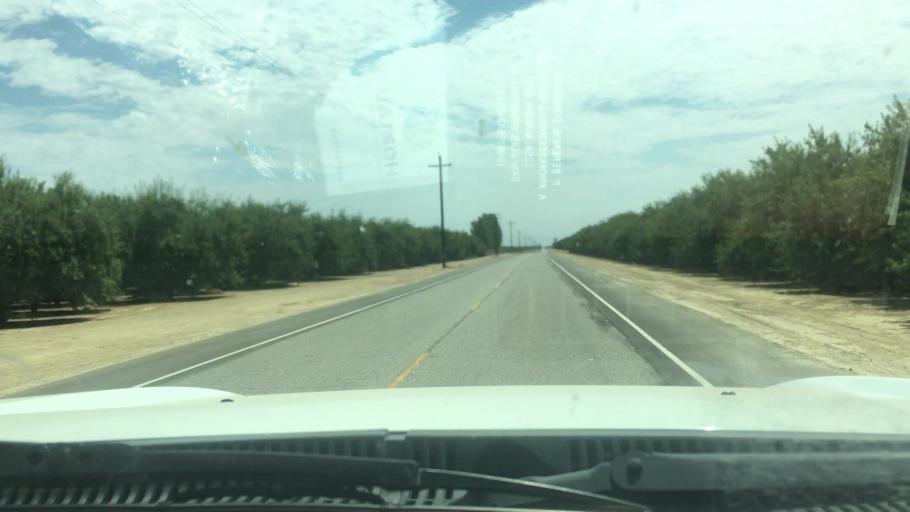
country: US
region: California
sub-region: Kern County
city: Wasco
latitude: 35.5579
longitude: -119.4244
